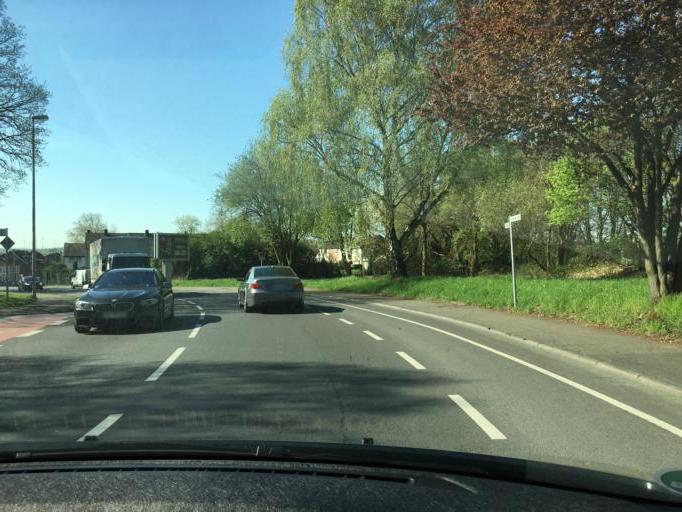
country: DE
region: North Rhine-Westphalia
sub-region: Regierungsbezirk Dusseldorf
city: Monchengladbach
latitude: 51.1536
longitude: 6.4342
